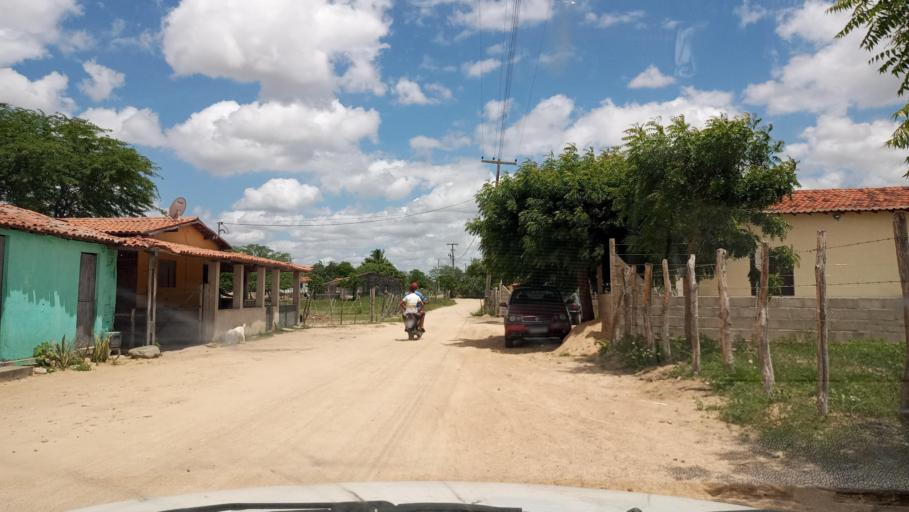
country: BR
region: Rio Grande do Norte
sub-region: Sao Jose Do Campestre
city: Sao Jose do Campestre
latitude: -6.4444
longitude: -35.6275
